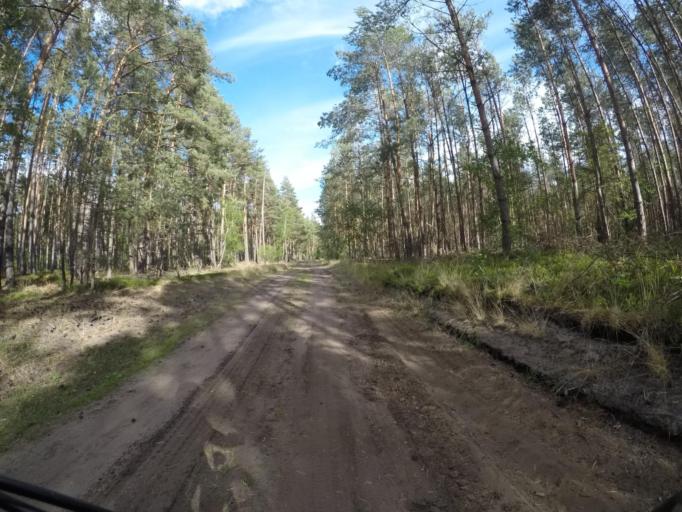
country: DE
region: Lower Saxony
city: Neu Darchau
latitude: 53.2723
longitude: 10.9732
